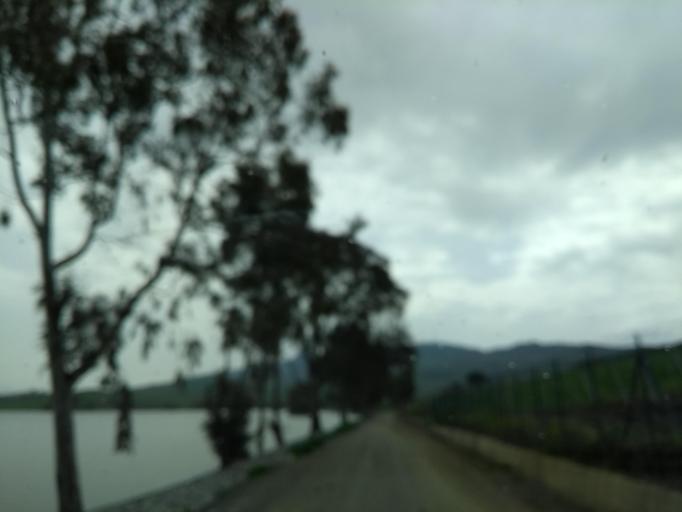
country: IT
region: Sicily
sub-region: Palermo
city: Partinico
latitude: 37.9942
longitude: 13.0822
